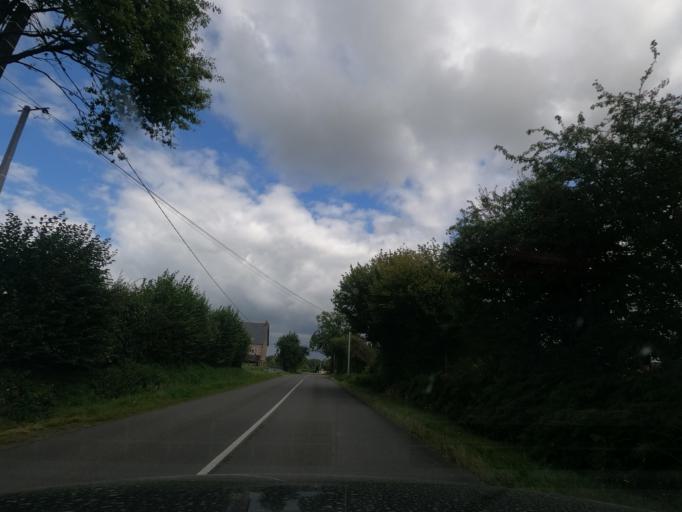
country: FR
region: Lower Normandy
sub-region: Departement de l'Orne
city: La Ferriere-aux-Etangs
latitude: 48.6886
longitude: -0.4648
